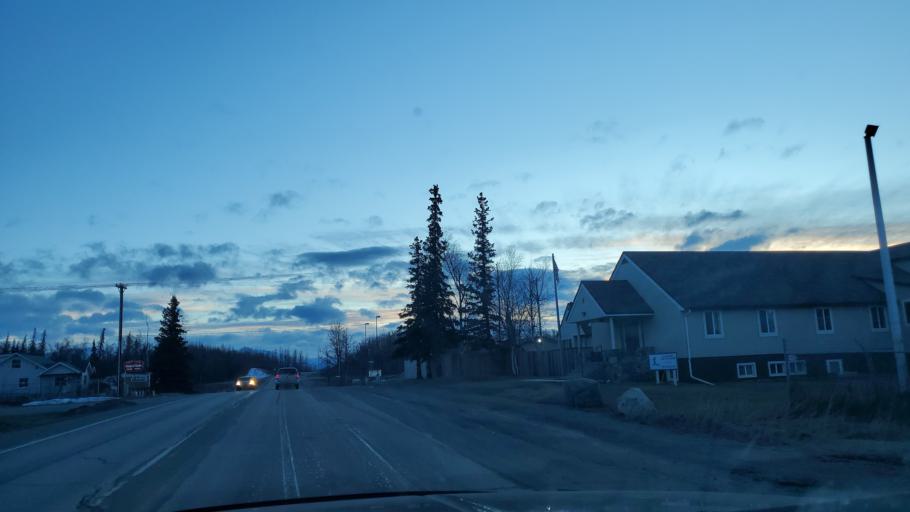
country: US
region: Alaska
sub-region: Matanuska-Susitna Borough
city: Wasilla
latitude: 61.5785
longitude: -149.4415
